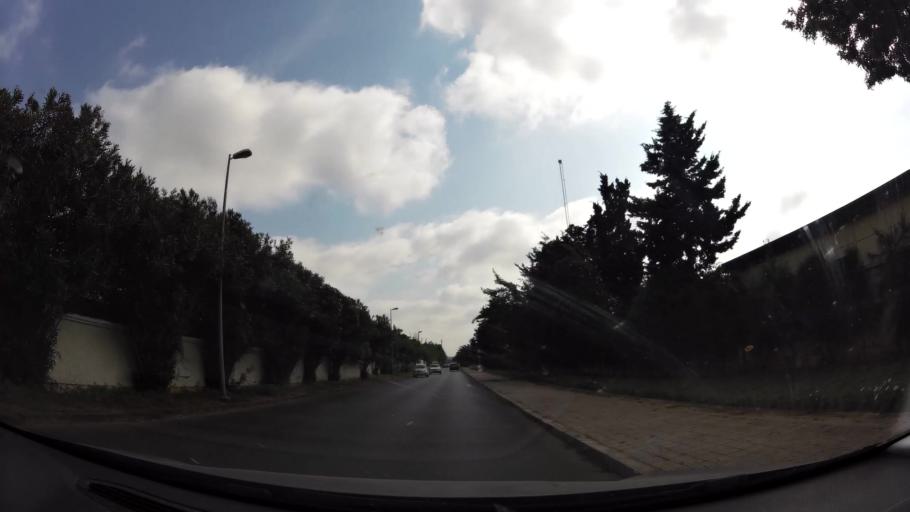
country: MA
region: Rabat-Sale-Zemmour-Zaer
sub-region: Rabat
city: Rabat
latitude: 33.9735
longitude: -6.8548
